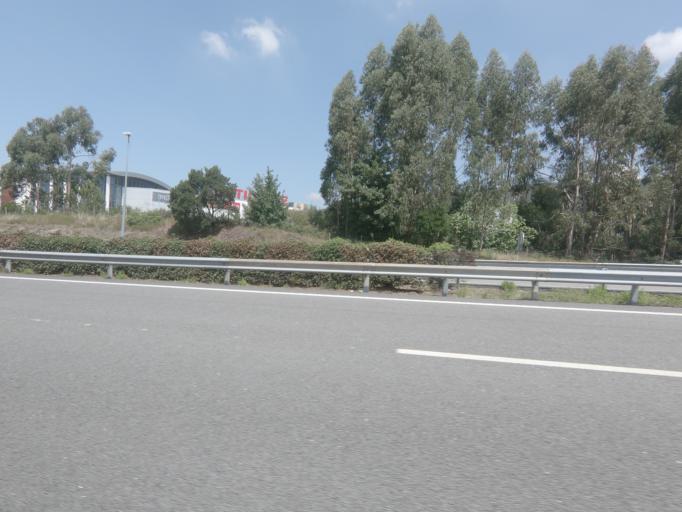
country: PT
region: Porto
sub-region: Valongo
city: Valongo
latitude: 41.1964
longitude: -8.4901
